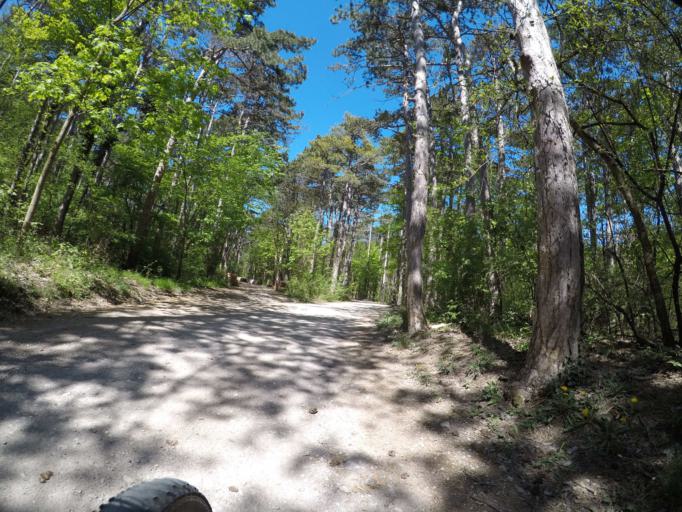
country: AT
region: Lower Austria
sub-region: Politischer Bezirk Modling
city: Modling
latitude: 48.0747
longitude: 16.2770
